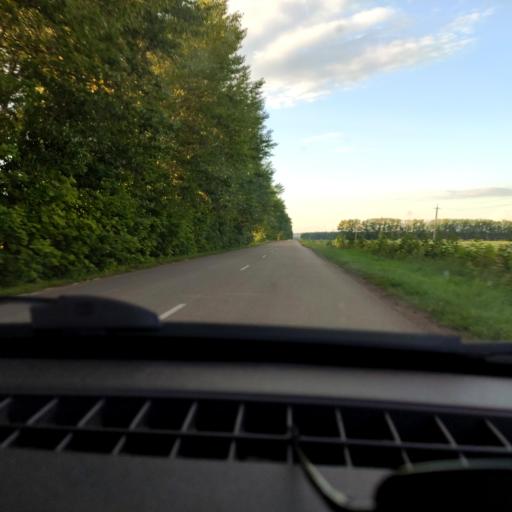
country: RU
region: Bashkortostan
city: Avdon
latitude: 54.5078
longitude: 55.6223
